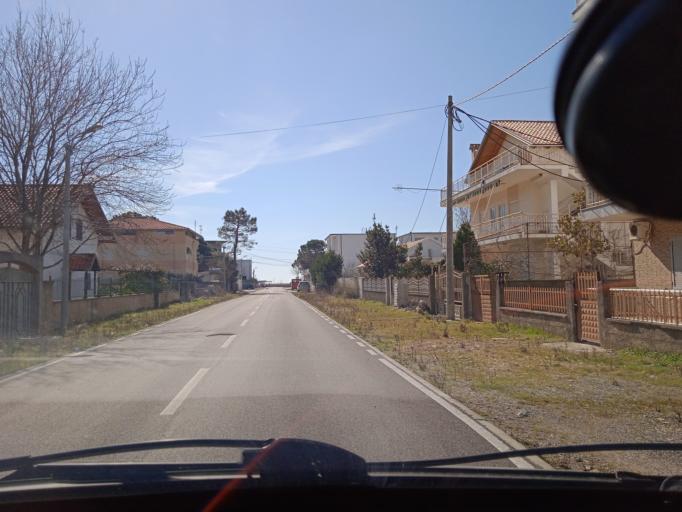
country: AL
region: Shkoder
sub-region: Rrethi i Shkodres
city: Velipoje
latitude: 41.8650
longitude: 19.4104
